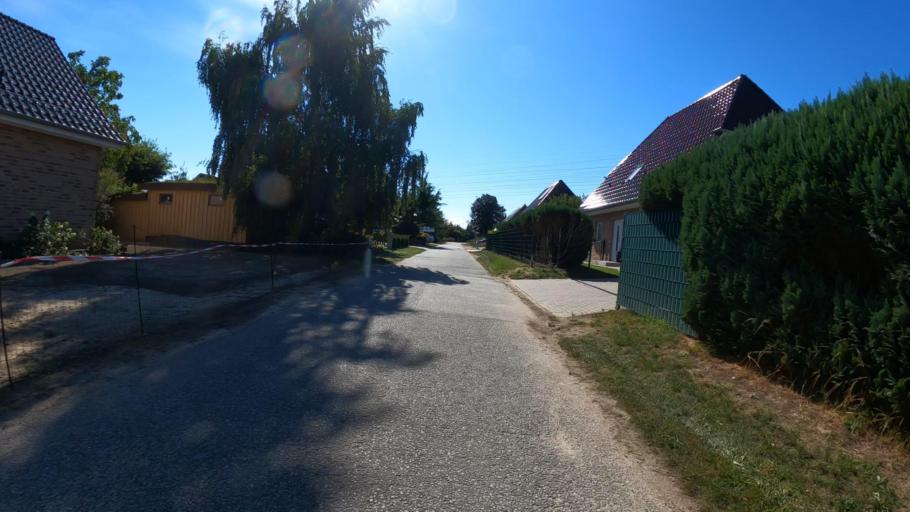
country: DE
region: Schleswig-Holstein
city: Hamberge
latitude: 53.8221
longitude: 10.6008
